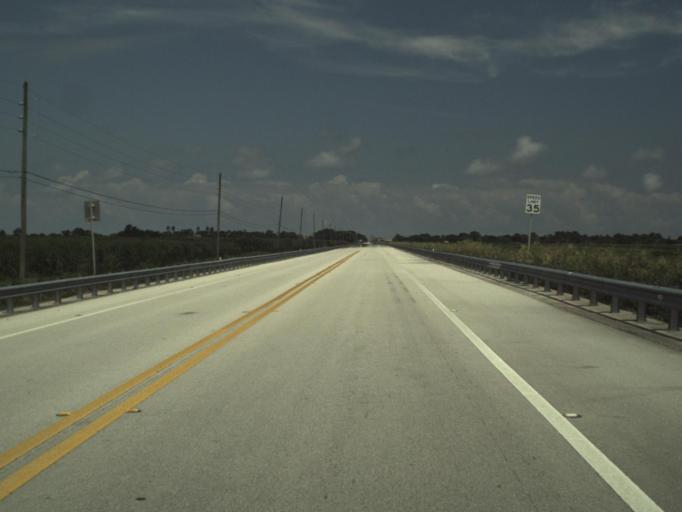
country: US
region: Florida
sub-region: Palm Beach County
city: Pahokee
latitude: 26.8539
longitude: -80.6182
